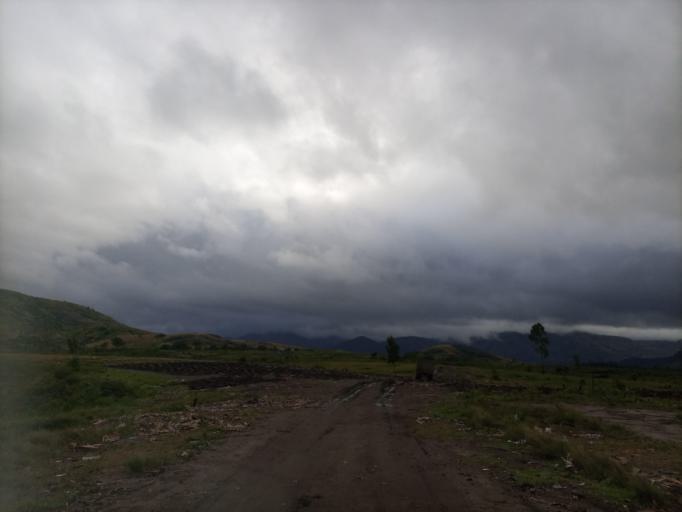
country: MG
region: Anosy
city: Fort Dauphin
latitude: -24.7605
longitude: 47.0728
